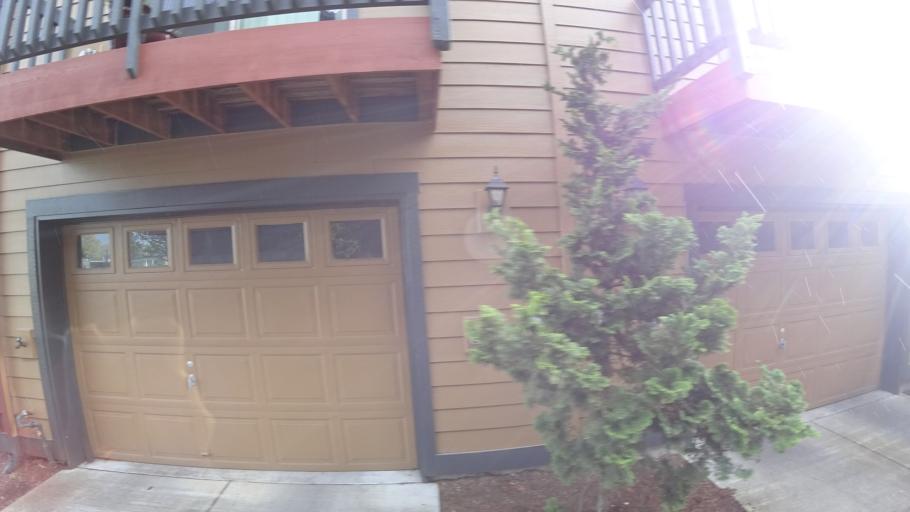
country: US
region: Oregon
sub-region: Washington County
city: Hillsboro
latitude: 45.5483
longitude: -122.9668
